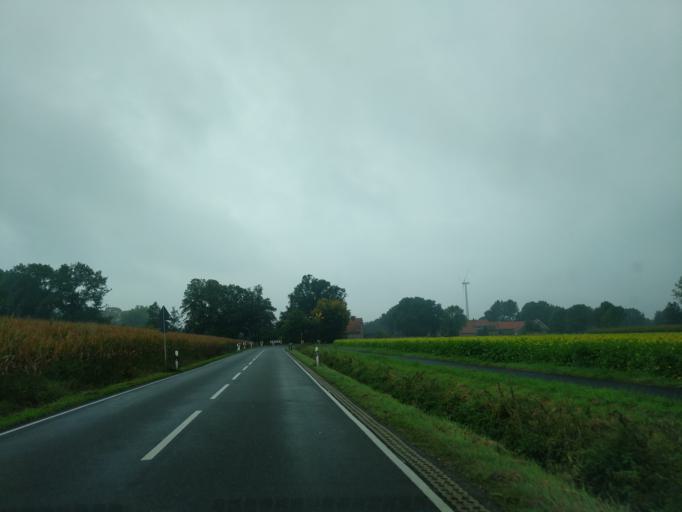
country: DE
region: North Rhine-Westphalia
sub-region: Regierungsbezirk Munster
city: Altenberge
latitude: 52.0282
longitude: 7.4504
